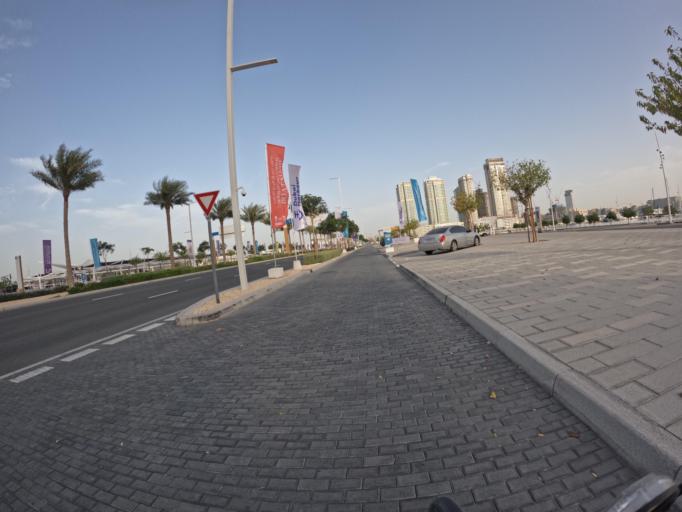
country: AE
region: Dubai
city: Dubai
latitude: 25.0920
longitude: 55.1442
